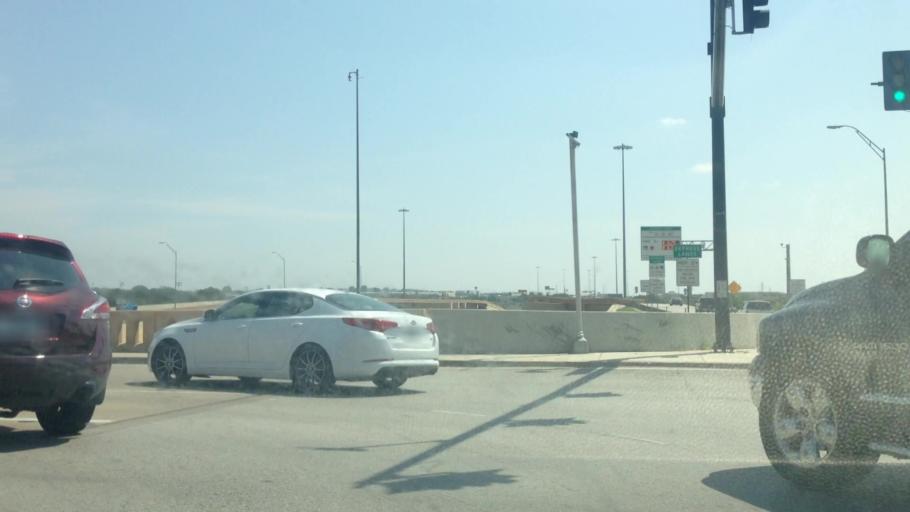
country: US
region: Texas
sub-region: Tarrant County
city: Watauga
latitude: 32.8392
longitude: -97.2642
